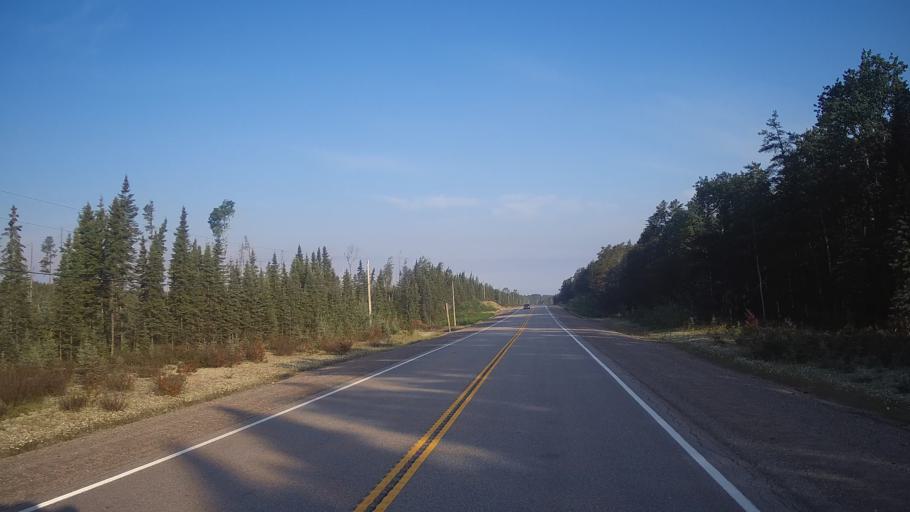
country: CA
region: Ontario
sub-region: Rainy River District
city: Atikokan
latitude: 49.3462
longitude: -91.4981
